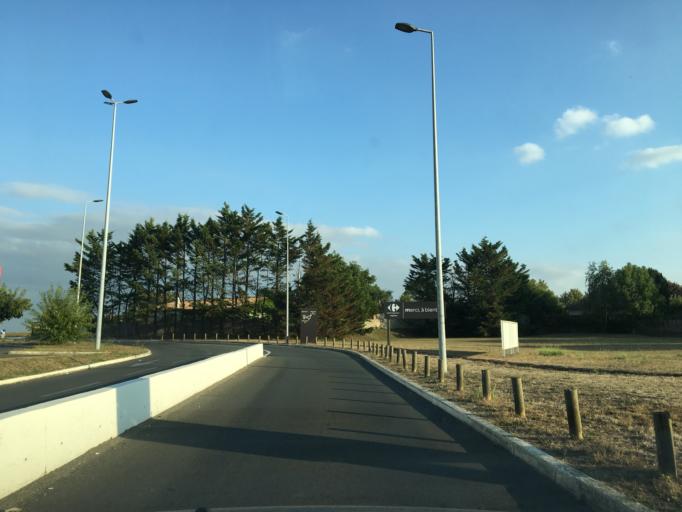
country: FR
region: Poitou-Charentes
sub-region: Departement de la Charente-Maritime
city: Angoulins
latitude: 46.1106
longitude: -1.1024
